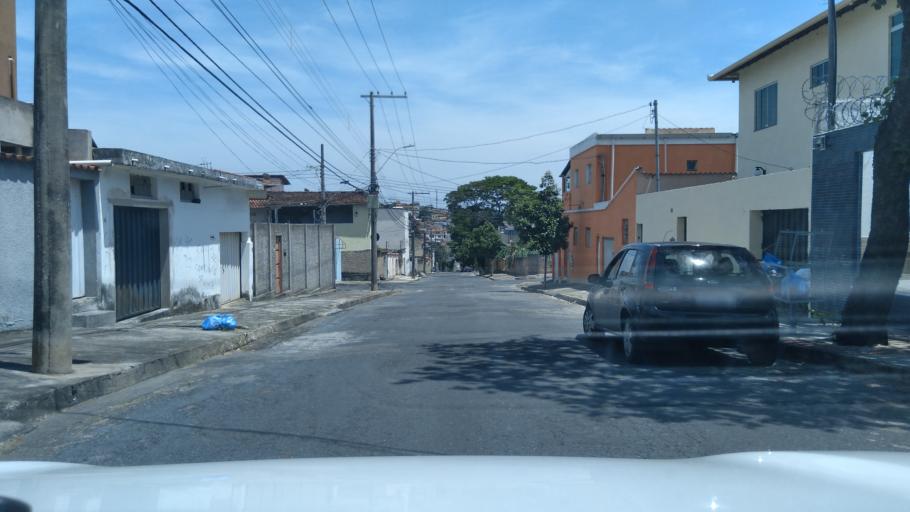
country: BR
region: Minas Gerais
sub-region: Contagem
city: Contagem
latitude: -19.8996
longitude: -44.0136
